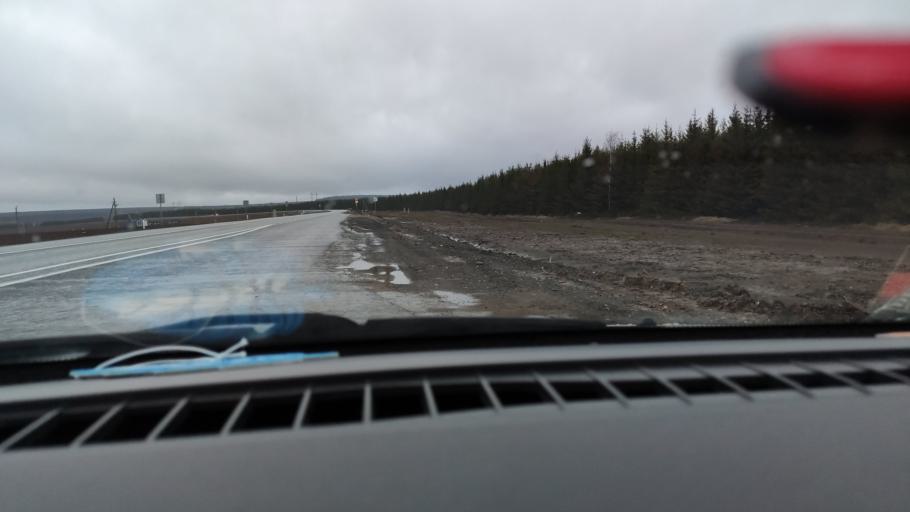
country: RU
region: Udmurtiya
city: Alnashi
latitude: 56.0842
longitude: 52.4143
